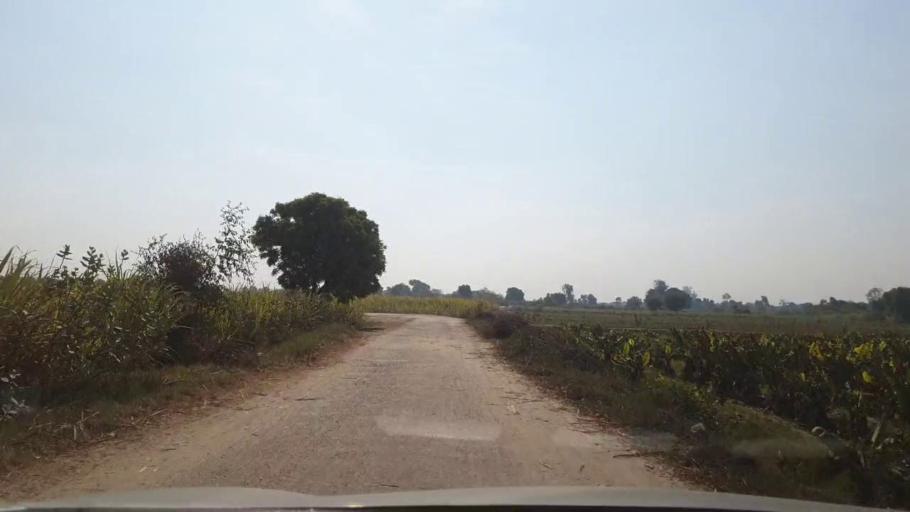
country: PK
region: Sindh
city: Tando Adam
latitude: 25.6276
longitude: 68.7342
